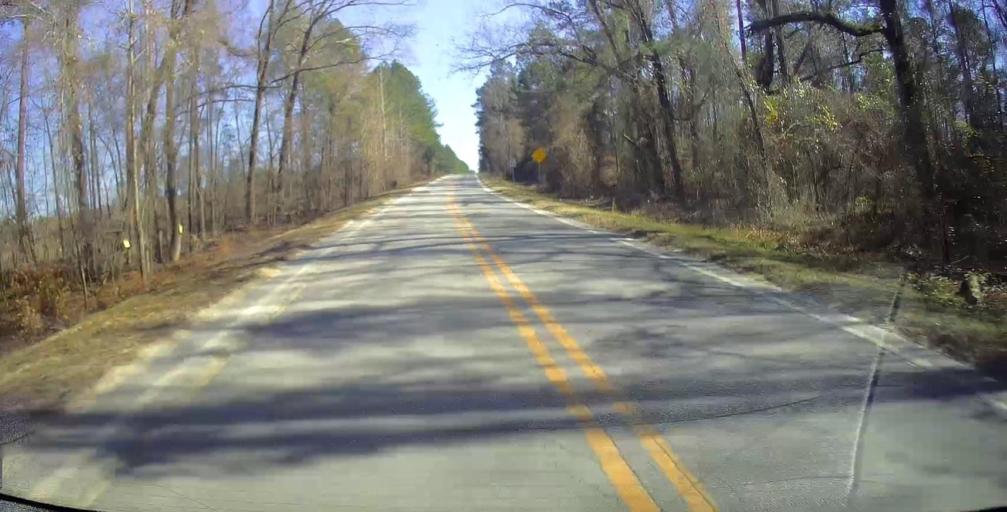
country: US
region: Georgia
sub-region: Crawford County
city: Roberta
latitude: 32.6384
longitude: -84.0004
